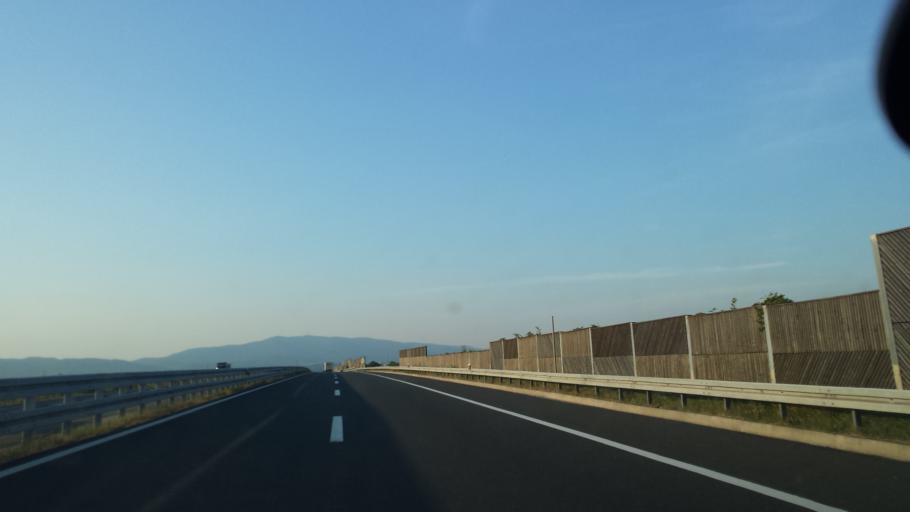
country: HR
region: Grad Zagreb
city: Brezovica
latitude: 45.7362
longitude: 15.8772
